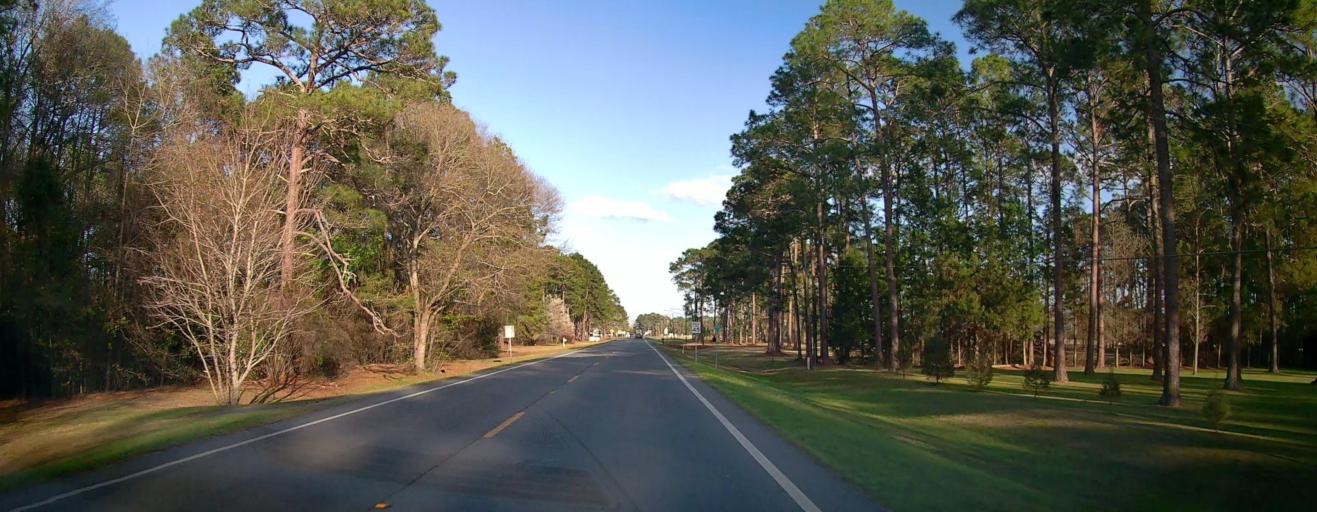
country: US
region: Georgia
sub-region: Evans County
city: Claxton
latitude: 32.1497
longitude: -81.9792
